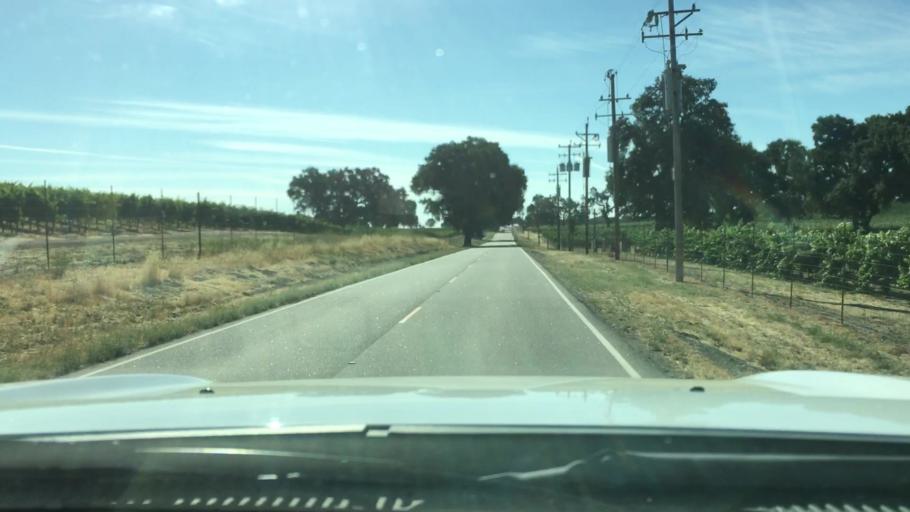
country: US
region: California
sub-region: San Luis Obispo County
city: Atascadero
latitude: 35.5544
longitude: -120.6189
